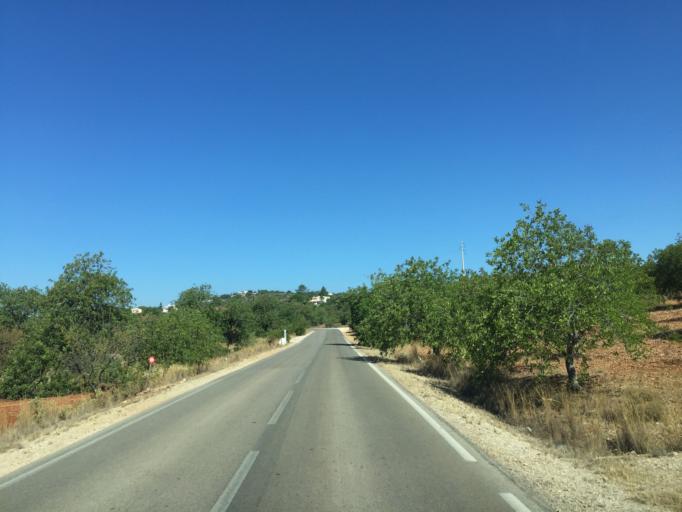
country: PT
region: Faro
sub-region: Loule
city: Vilamoura
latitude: 37.1147
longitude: -8.0761
